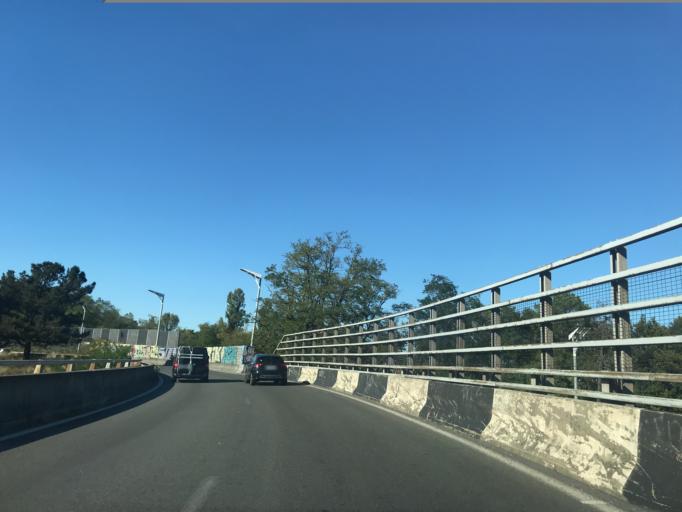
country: FR
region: Aquitaine
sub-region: Departement de la Gironde
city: Gradignan
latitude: 44.7887
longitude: -0.6230
